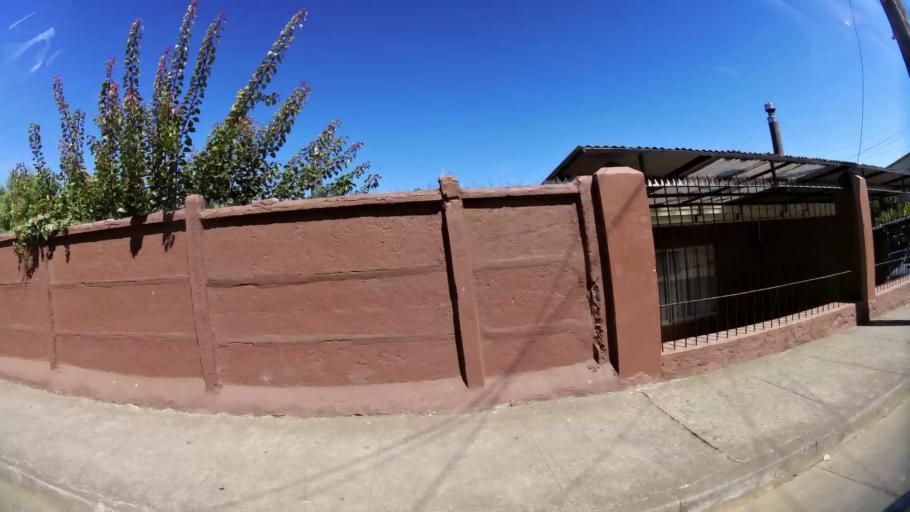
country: CL
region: Biobio
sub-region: Provincia de Concepcion
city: Penco
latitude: -36.7326
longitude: -72.9883
